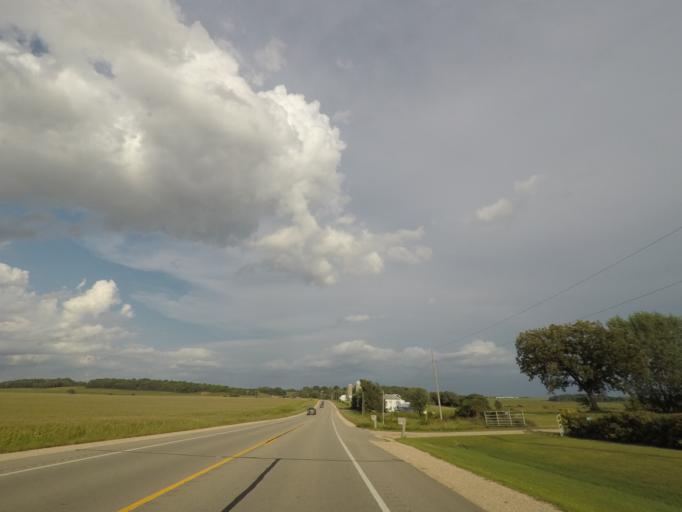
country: US
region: Wisconsin
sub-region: Dane County
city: Waunakee
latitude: 43.1919
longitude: -89.5204
